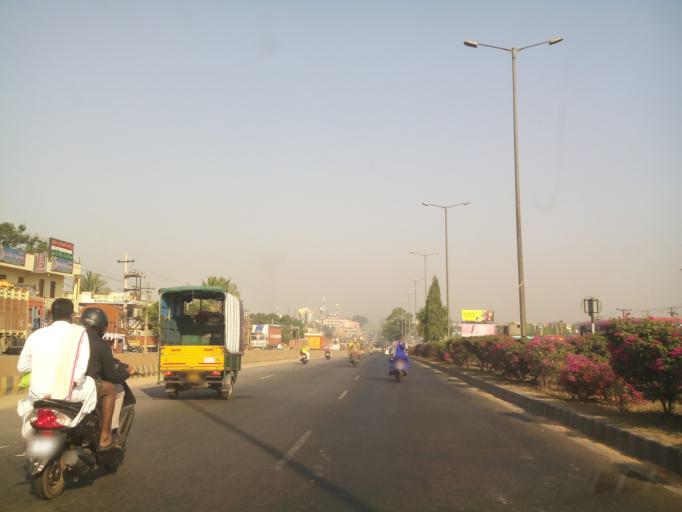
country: IN
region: Karnataka
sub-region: Bangalore Rural
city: Nelamangala
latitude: 13.0619
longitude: 77.4599
